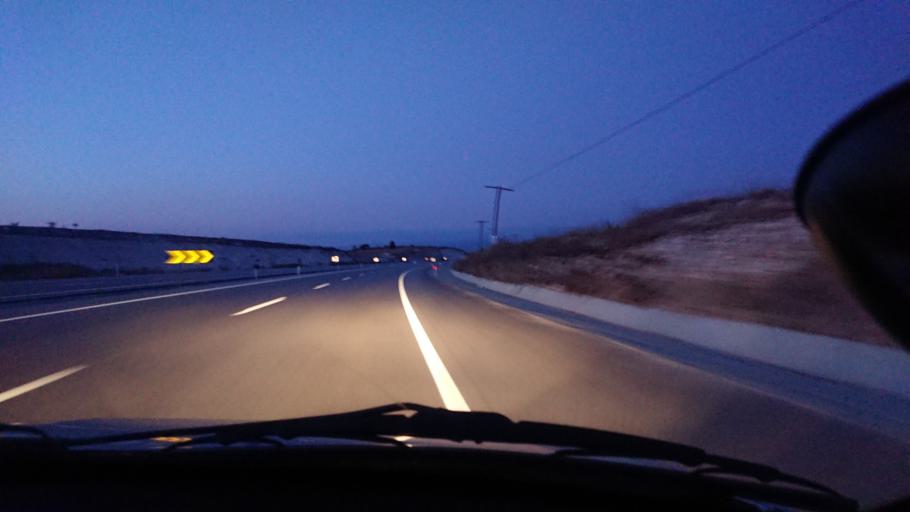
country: TR
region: Kuetahya
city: Cavdarhisar
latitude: 39.1665
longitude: 29.5944
